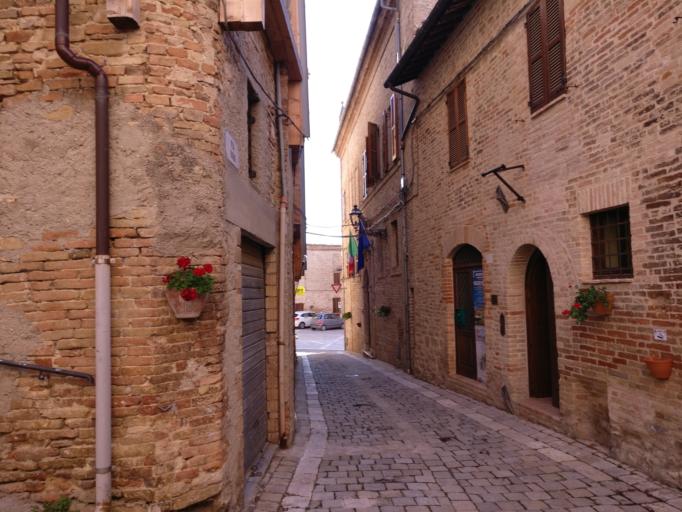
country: IT
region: The Marches
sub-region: Provincia di Ascoli Piceno
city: Montedinove
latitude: 42.9707
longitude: 13.5867
